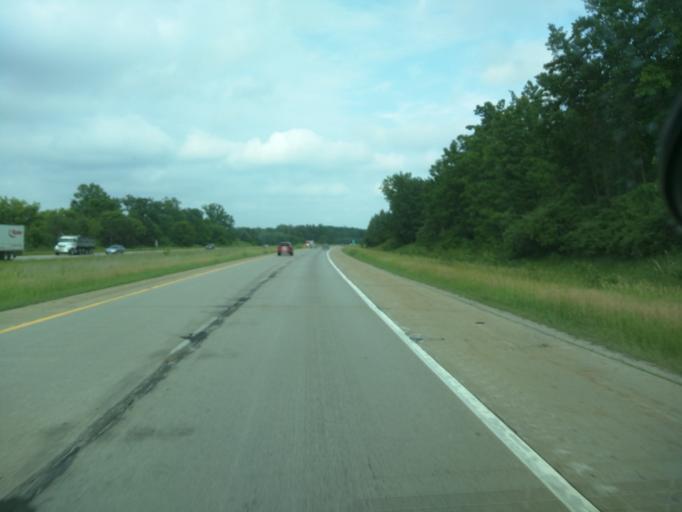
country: US
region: Michigan
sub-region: Clinton County
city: Bath
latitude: 42.8031
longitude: -84.4753
